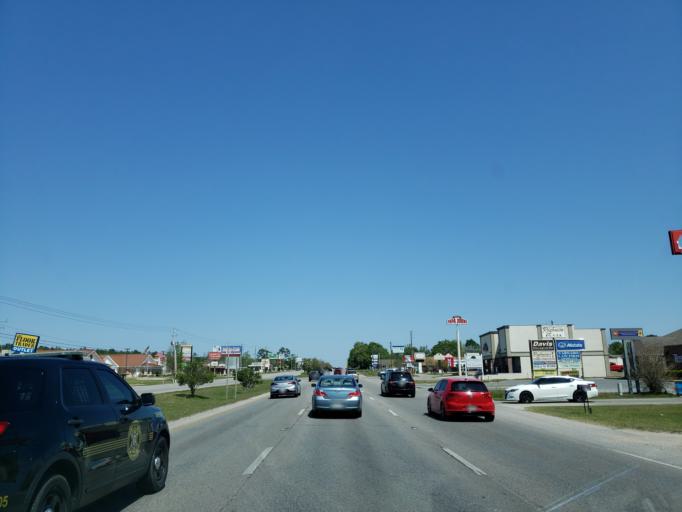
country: US
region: Mississippi
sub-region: Harrison County
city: Lyman
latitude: 30.4608
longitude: -89.1011
